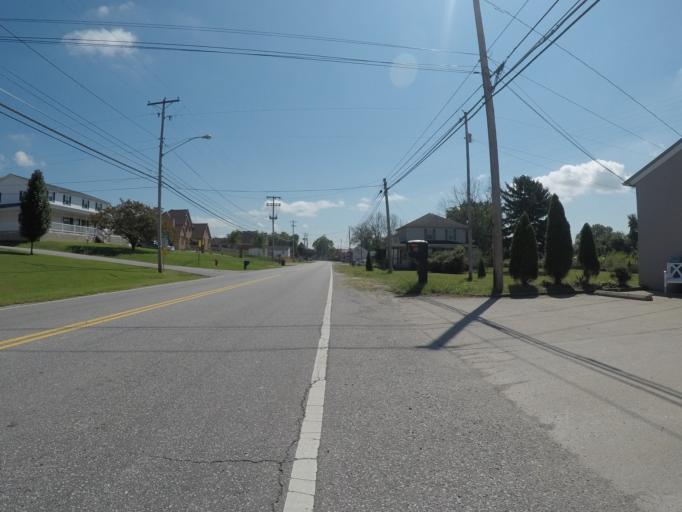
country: US
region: Ohio
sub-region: Lawrence County
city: South Point
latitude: 38.4138
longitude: -82.5816
